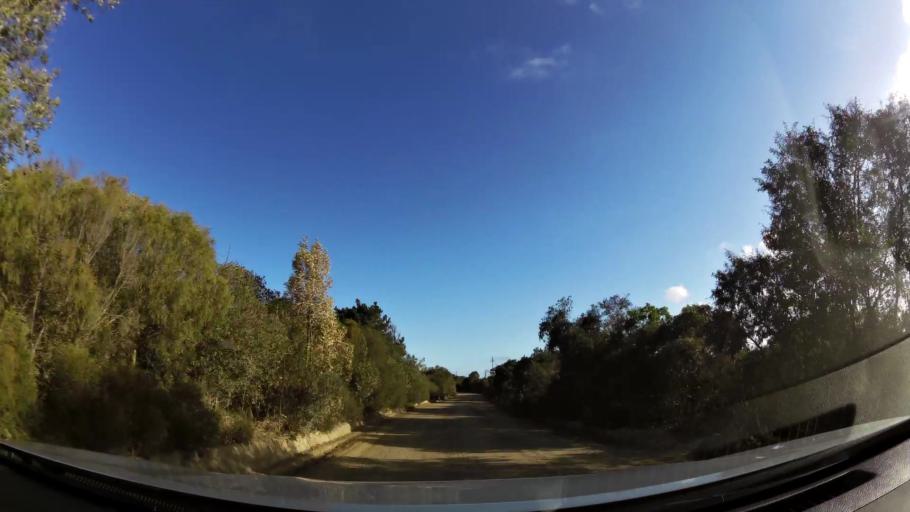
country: ZA
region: Western Cape
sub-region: Eden District Municipality
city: George
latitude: -33.9909
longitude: 22.5632
